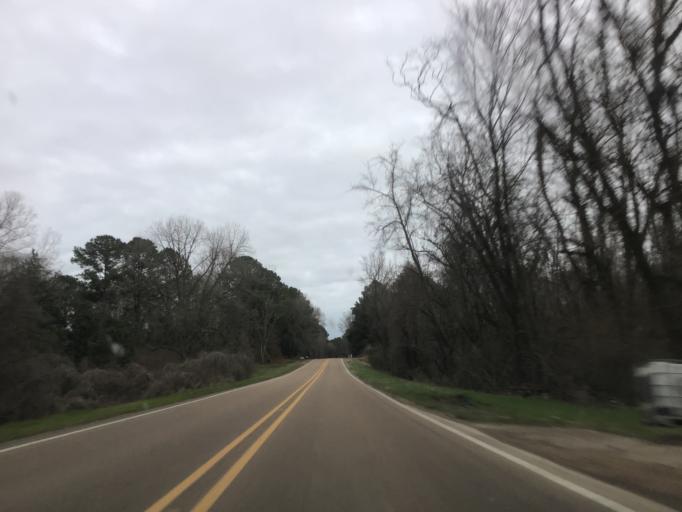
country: US
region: Mississippi
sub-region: Warren County
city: Beechwood
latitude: 32.2801
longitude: -90.7808
